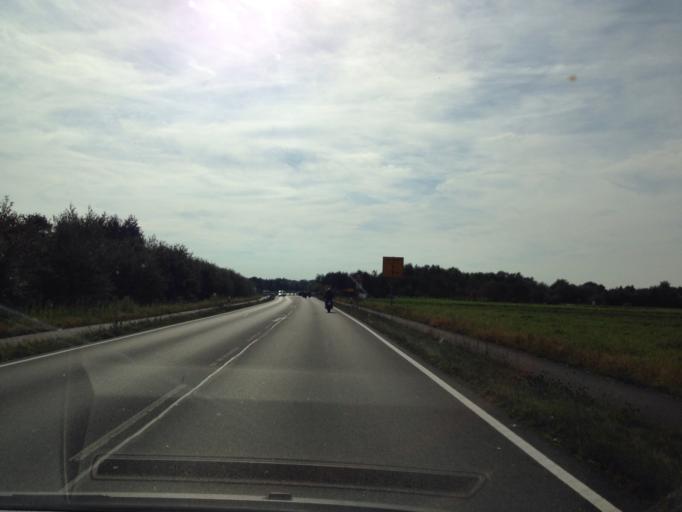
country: DE
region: North Rhine-Westphalia
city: Ludinghausen
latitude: 51.7749
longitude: 7.4741
